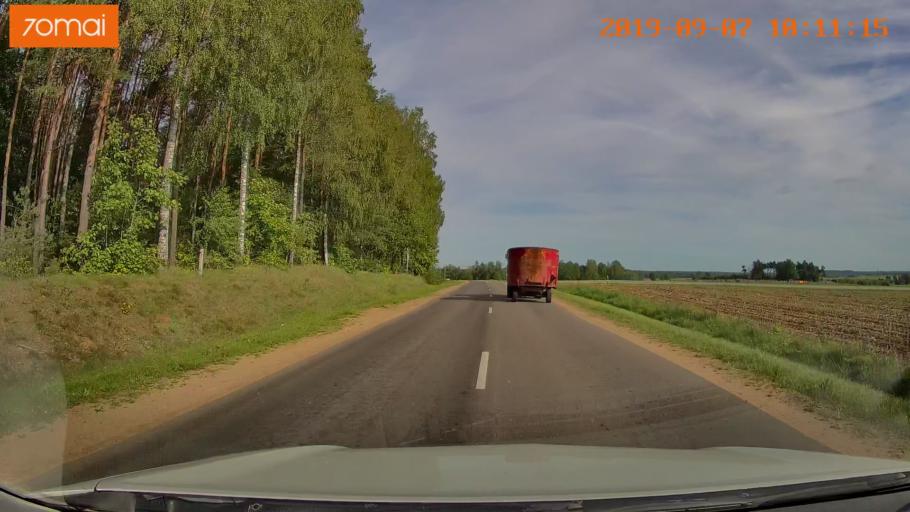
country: BY
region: Grodnenskaya
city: Voranava
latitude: 54.1201
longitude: 25.3674
